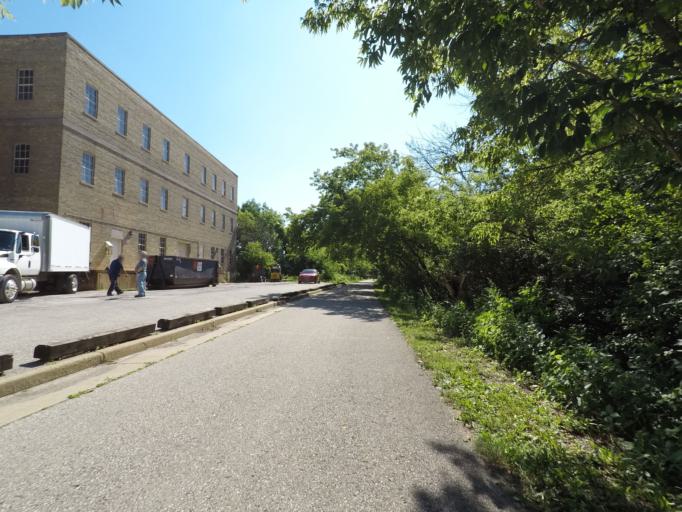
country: US
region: Wisconsin
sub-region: Milwaukee County
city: West Milwaukee
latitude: 43.0254
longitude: -87.9748
